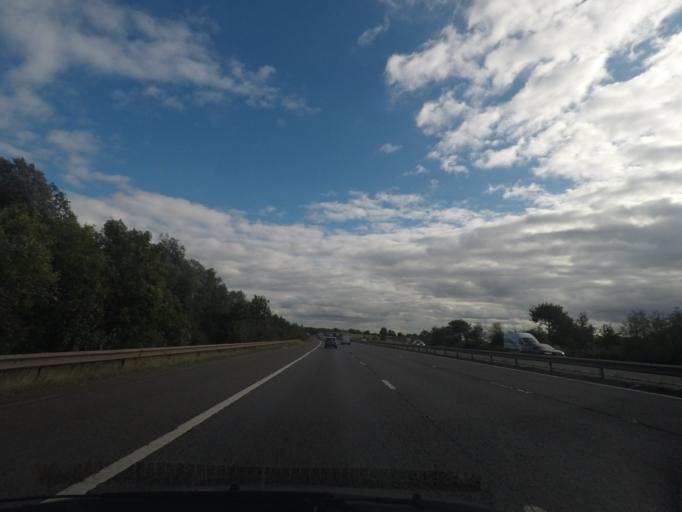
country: GB
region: England
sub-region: Leicestershire
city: Markfield
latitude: 52.6797
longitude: -1.2881
